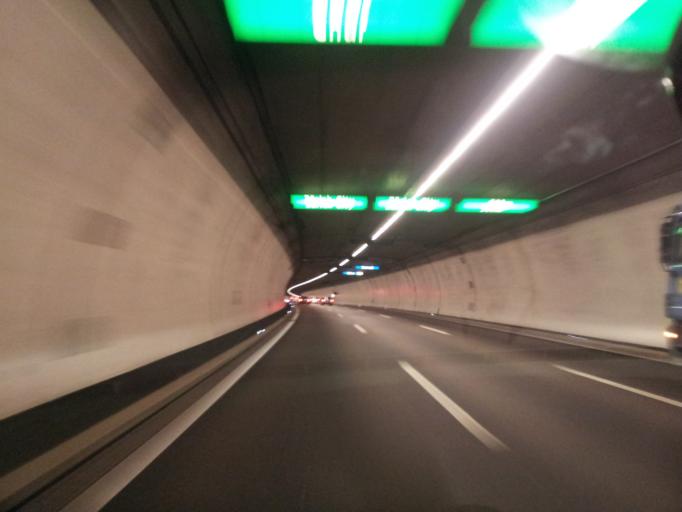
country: CH
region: Zurich
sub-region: Bezirk Dietikon
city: Birmensdorf
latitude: 47.3442
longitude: 8.4303
